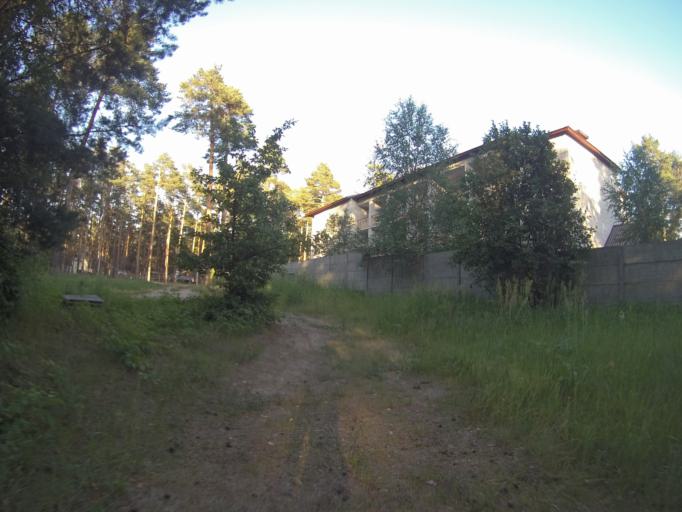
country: RU
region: Vladimir
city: Kommunar
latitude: 56.1423
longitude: 40.4895
